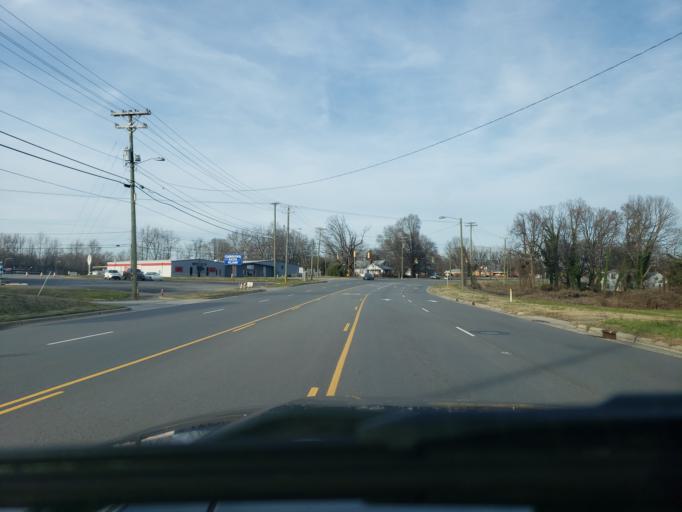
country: US
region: North Carolina
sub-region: Cleveland County
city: Shelby
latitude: 35.2743
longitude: -81.4968
